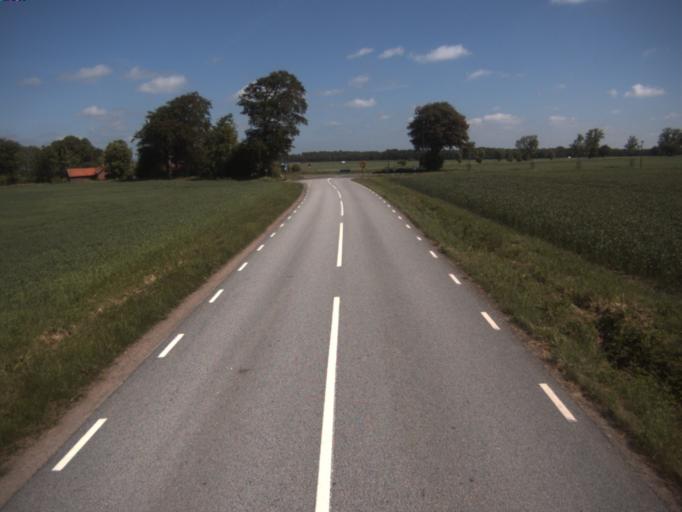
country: DK
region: Capital Region
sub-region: Helsingor Kommune
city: Helsingor
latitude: 56.1051
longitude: 12.6390
